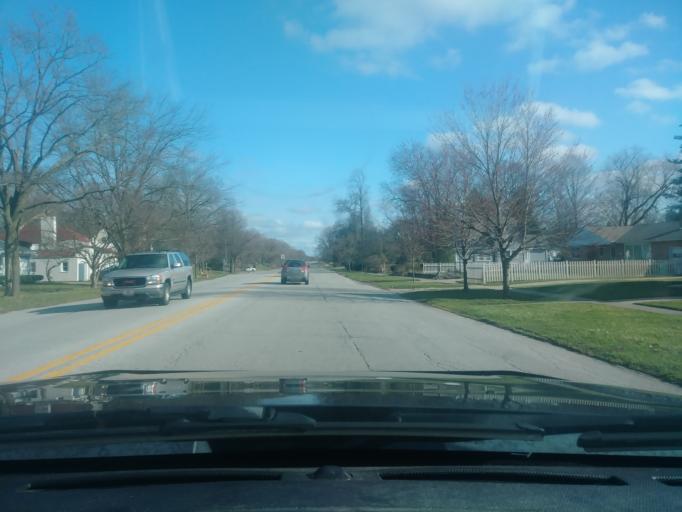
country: US
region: Indiana
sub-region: LaPorte County
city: LaPorte
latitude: 41.5972
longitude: -86.7101
